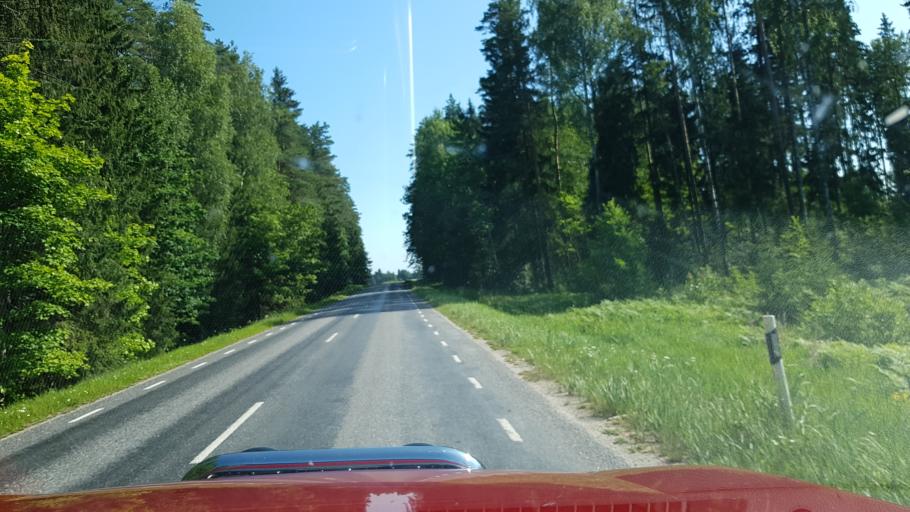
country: EE
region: Polvamaa
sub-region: Polva linn
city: Polva
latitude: 57.9946
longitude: 26.9081
